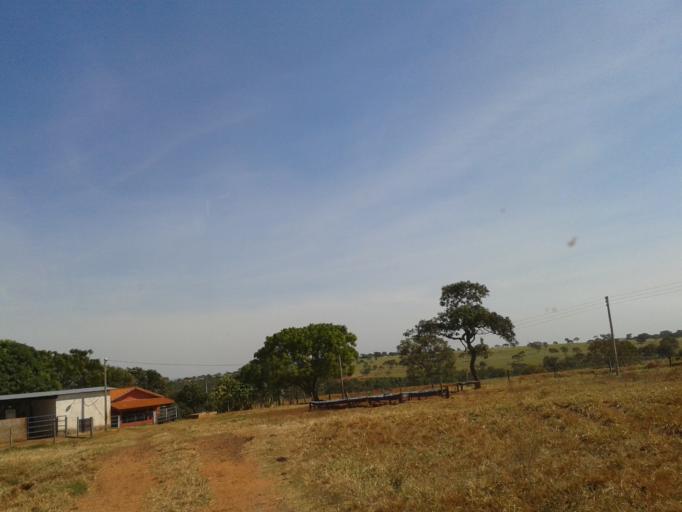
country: BR
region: Minas Gerais
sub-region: Campina Verde
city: Campina Verde
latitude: -19.4816
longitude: -49.5706
